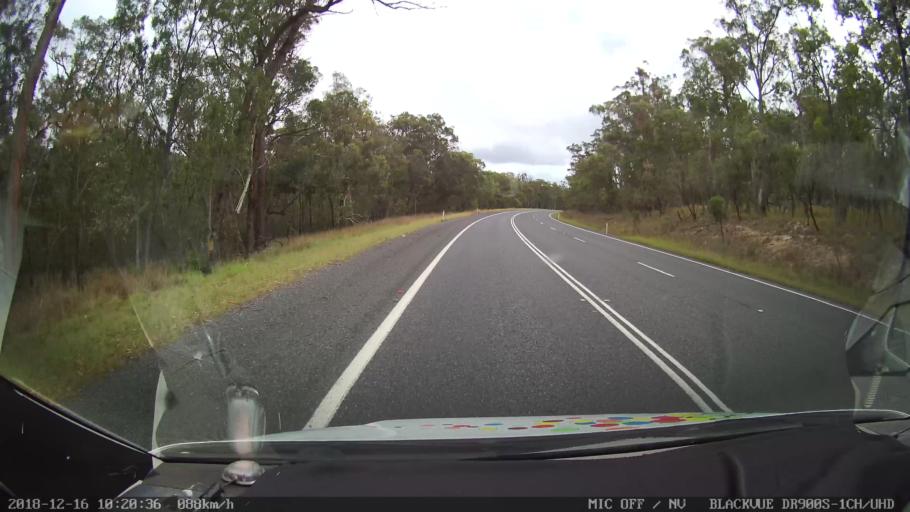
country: AU
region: New South Wales
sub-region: Tenterfield Municipality
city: Carrolls Creek
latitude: -29.2180
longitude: 152.0097
